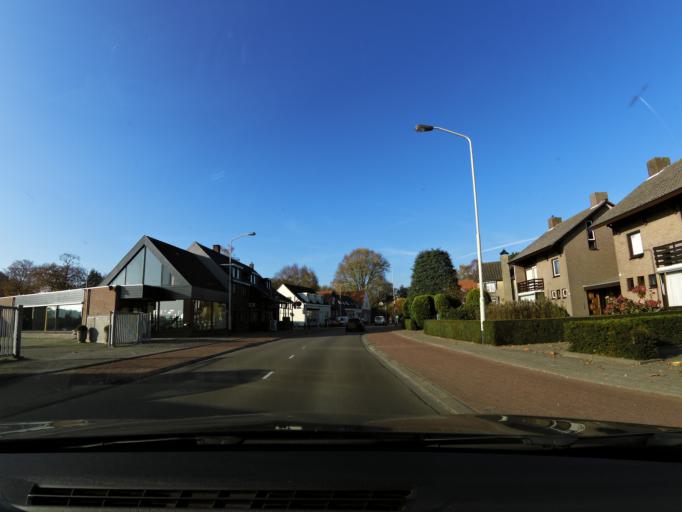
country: NL
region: North Brabant
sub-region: Gemeente Breda
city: Breda
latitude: 51.5571
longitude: 4.7925
